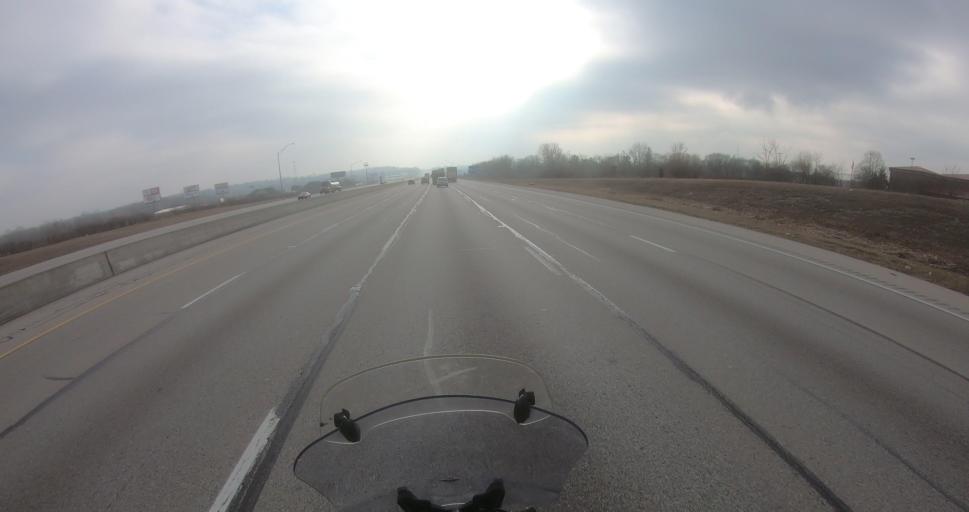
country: US
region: Ohio
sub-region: Warren County
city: Hunter
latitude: 39.5018
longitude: -84.3236
